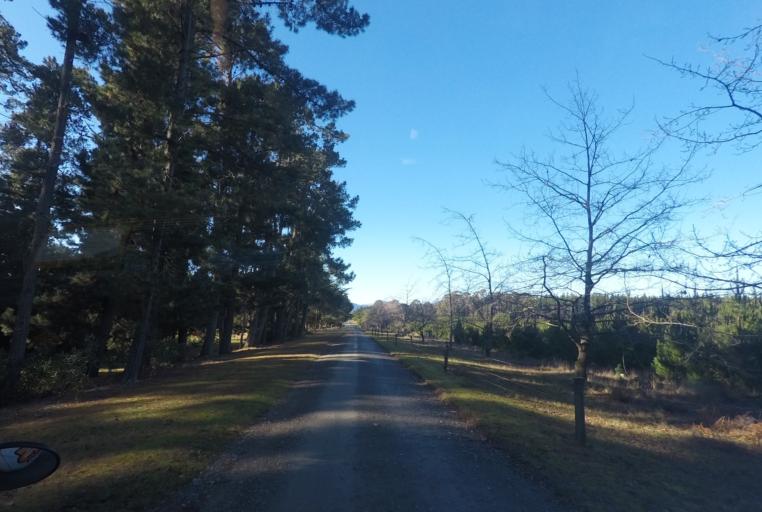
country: NZ
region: Tasman
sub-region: Tasman District
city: Mapua
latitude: -41.2655
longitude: 173.1447
